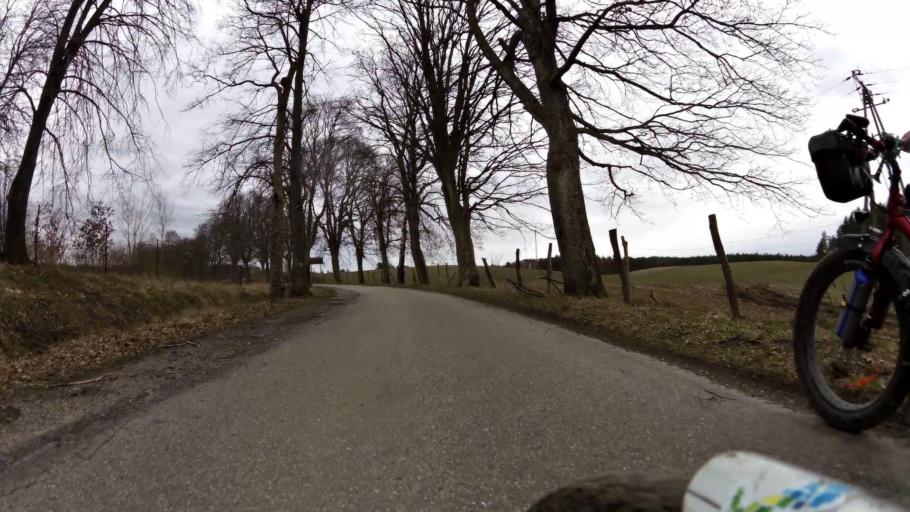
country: PL
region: Pomeranian Voivodeship
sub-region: Powiat bytowski
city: Trzebielino
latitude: 54.1036
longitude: 17.1296
